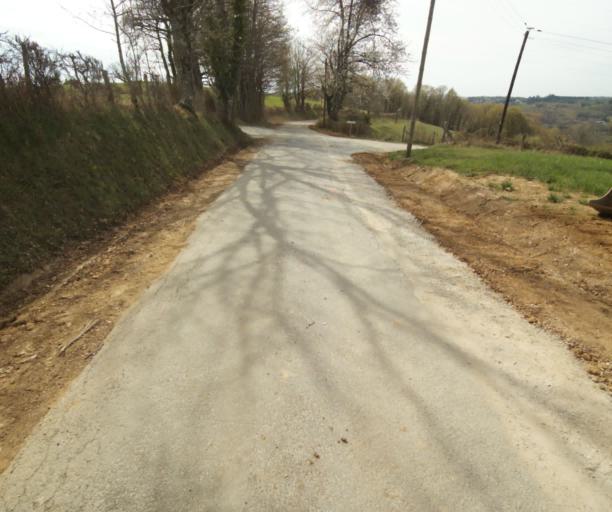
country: FR
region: Limousin
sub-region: Departement de la Correze
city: Naves
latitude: 45.2960
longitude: 1.7797
